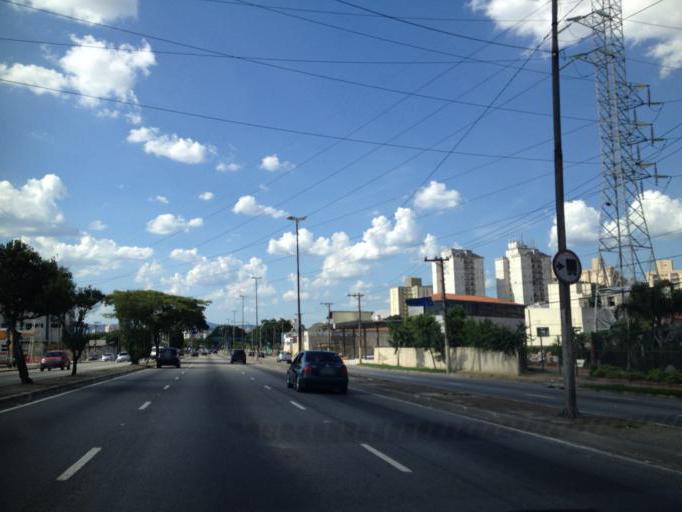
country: BR
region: Sao Paulo
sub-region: Sao Paulo
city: Sao Paulo
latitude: -23.5351
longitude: -46.5828
